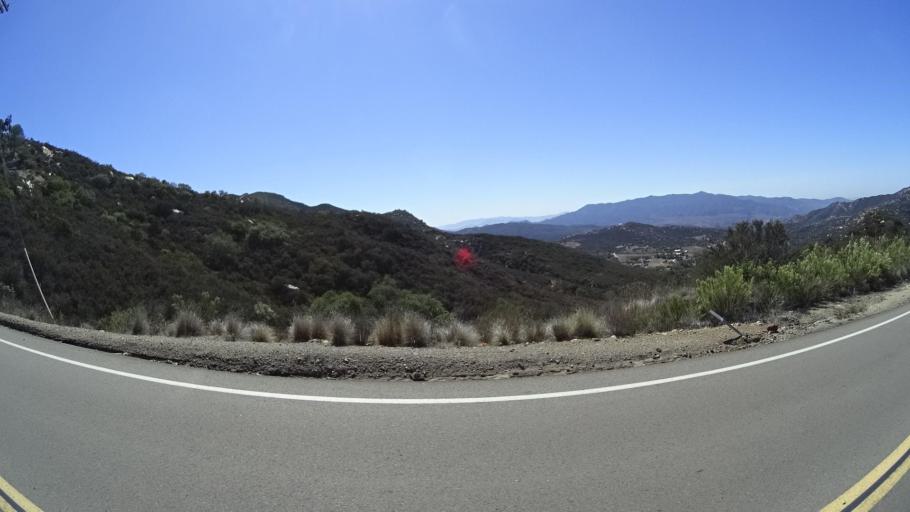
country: US
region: California
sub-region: San Diego County
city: Jamul
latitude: 32.7339
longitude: -116.8055
